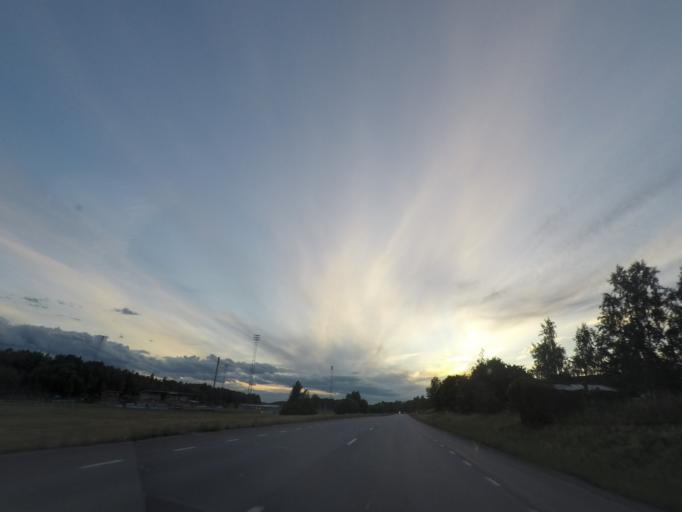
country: SE
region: Stockholm
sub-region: Sigtuna Kommun
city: Marsta
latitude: 59.6201
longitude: 17.8415
